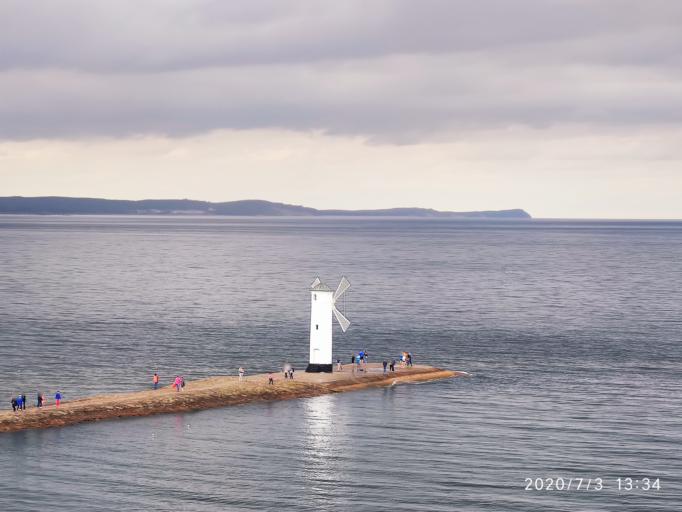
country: PL
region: West Pomeranian Voivodeship
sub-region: Swinoujscie
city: Swinoujscie
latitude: 53.9247
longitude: 14.2812
